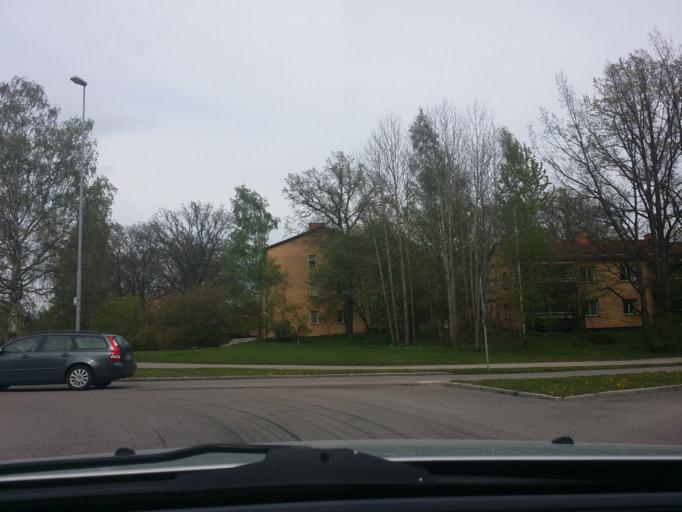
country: SE
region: Vaestmanland
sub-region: Vasteras
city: Vasteras
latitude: 59.6017
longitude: 16.5897
